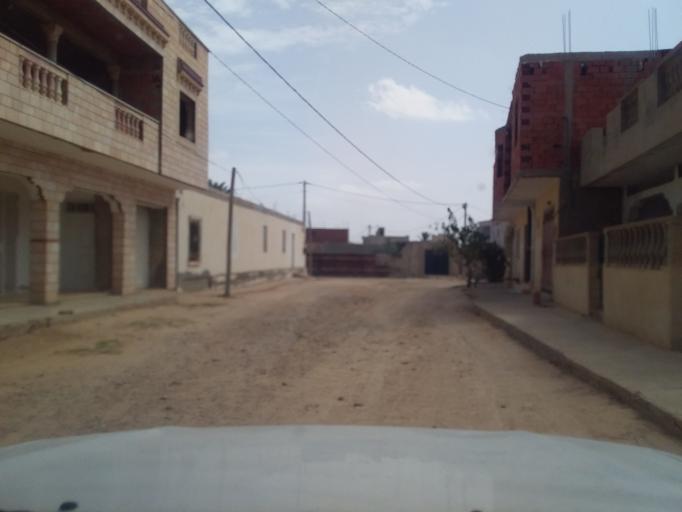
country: TN
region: Qabis
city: Matmata
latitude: 33.6158
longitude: 10.2756
